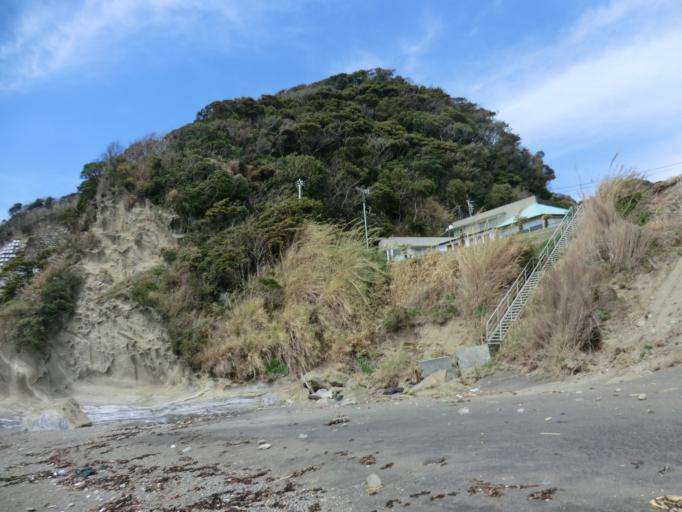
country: JP
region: Chiba
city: Futtsu
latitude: 35.1515
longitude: 139.8286
